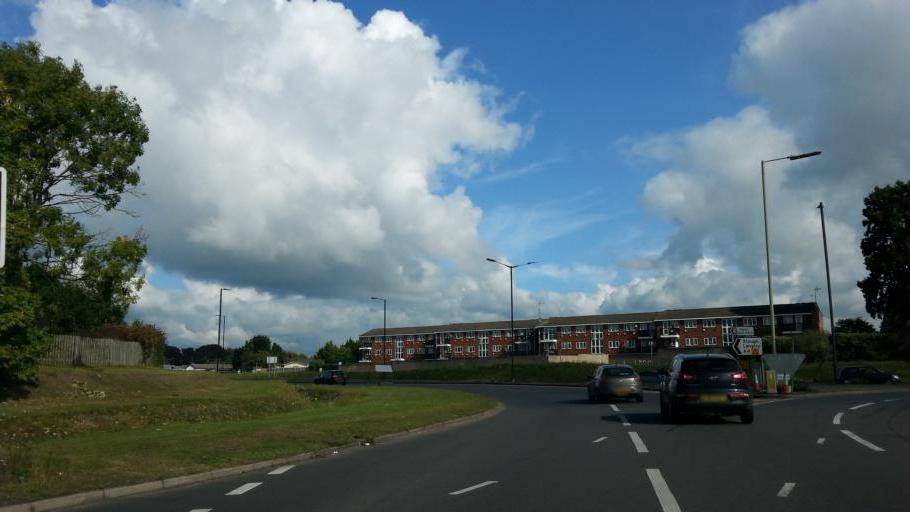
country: GB
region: England
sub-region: Royal Borough of Windsor and Maidenhead
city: Horton
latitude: 51.4918
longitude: -0.5444
